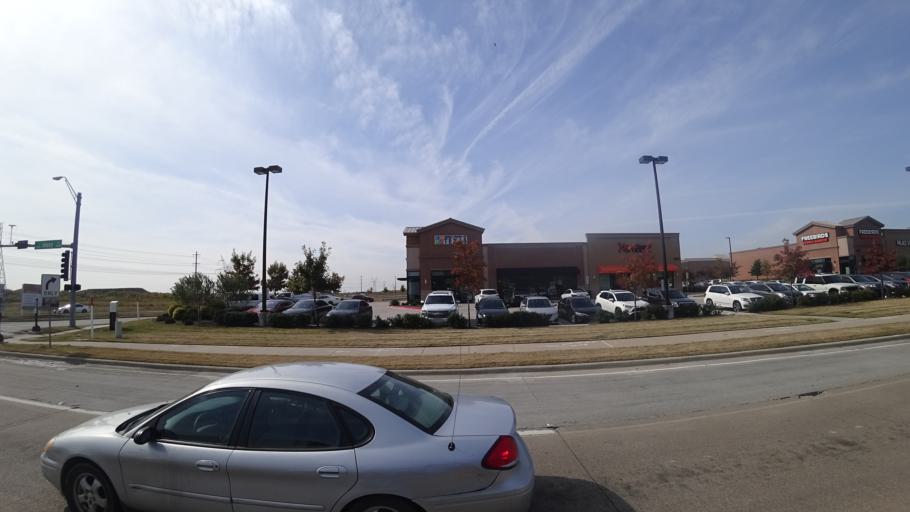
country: US
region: Texas
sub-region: Denton County
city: The Colony
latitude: 33.0622
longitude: -96.8869
